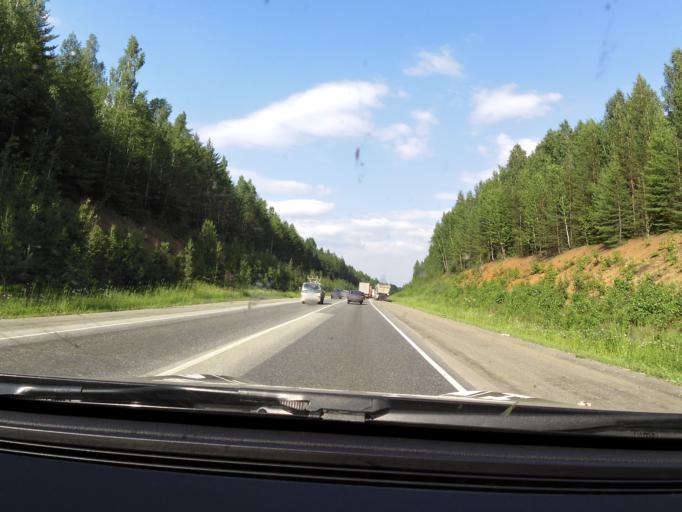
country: RU
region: Sverdlovsk
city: Talitsa
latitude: 56.8391
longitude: 60.0039
